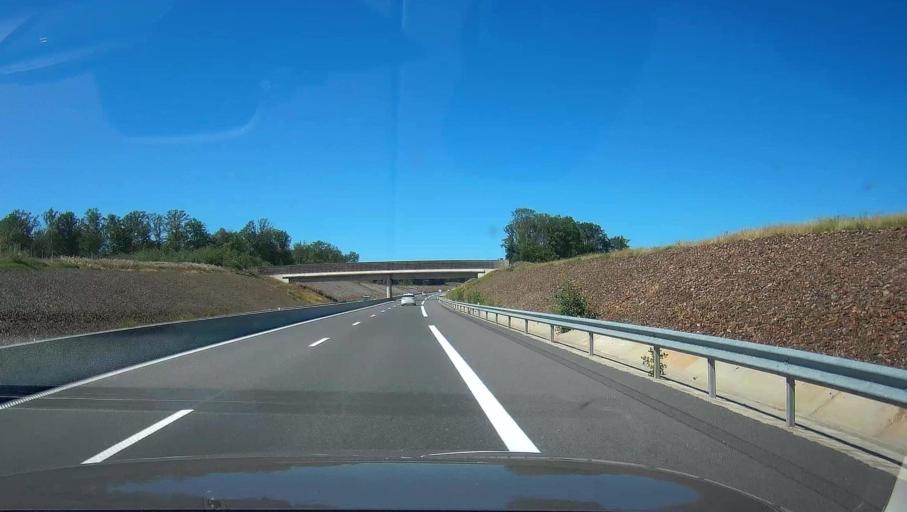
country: FR
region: Champagne-Ardenne
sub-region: Departement des Ardennes
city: Rimogne
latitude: 49.8140
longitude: 4.5185
